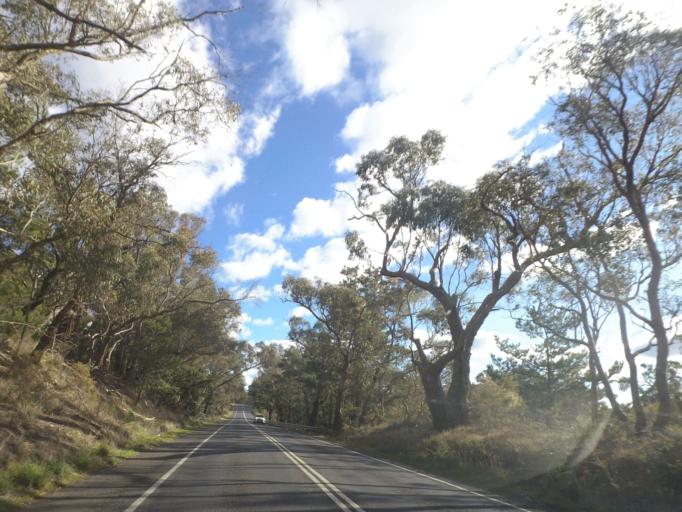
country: AU
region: Victoria
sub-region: Mount Alexander
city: Castlemaine
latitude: -37.1047
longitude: 144.3113
